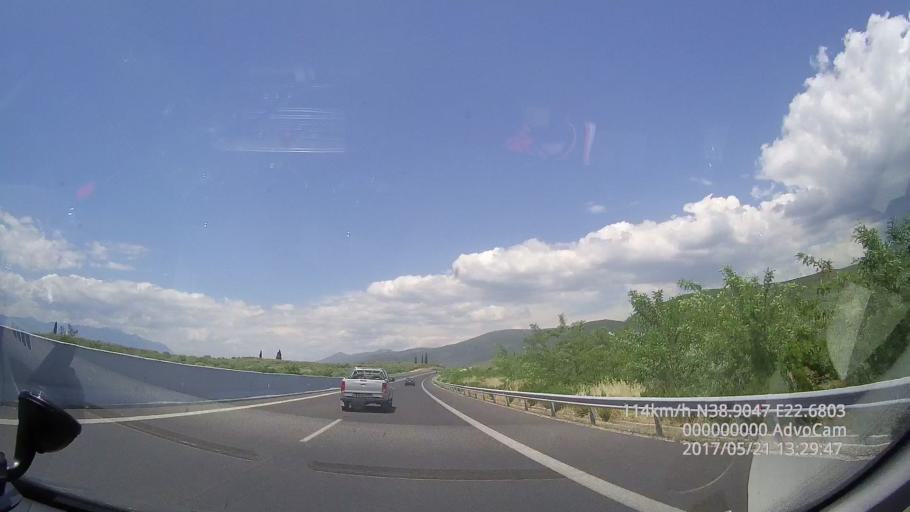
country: GR
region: Central Greece
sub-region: Nomos Fthiotidos
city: Stylida
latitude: 38.9048
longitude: 22.6796
